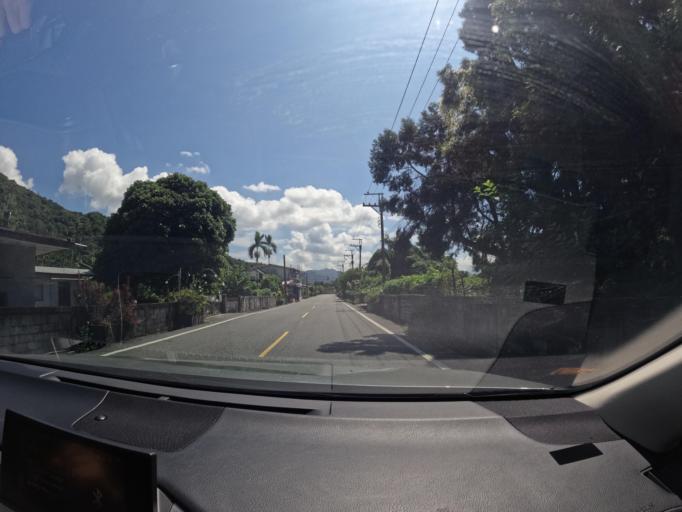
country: TW
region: Taiwan
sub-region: Hualien
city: Hualian
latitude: 23.5835
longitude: 121.3651
